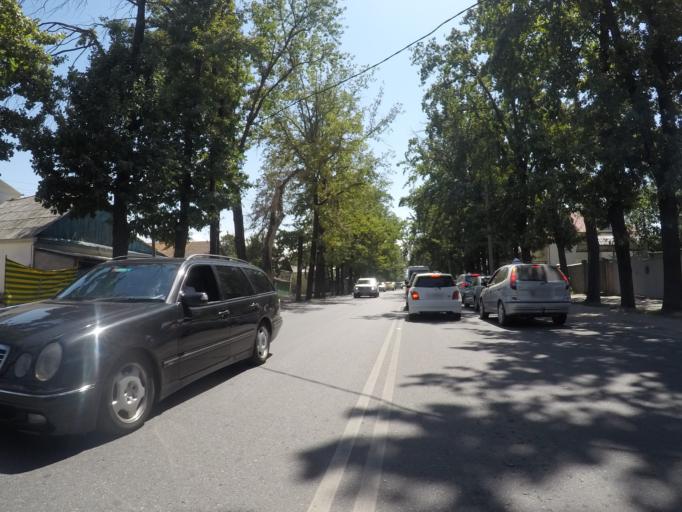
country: KG
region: Chuy
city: Bishkek
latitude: 42.8529
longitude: 74.5770
